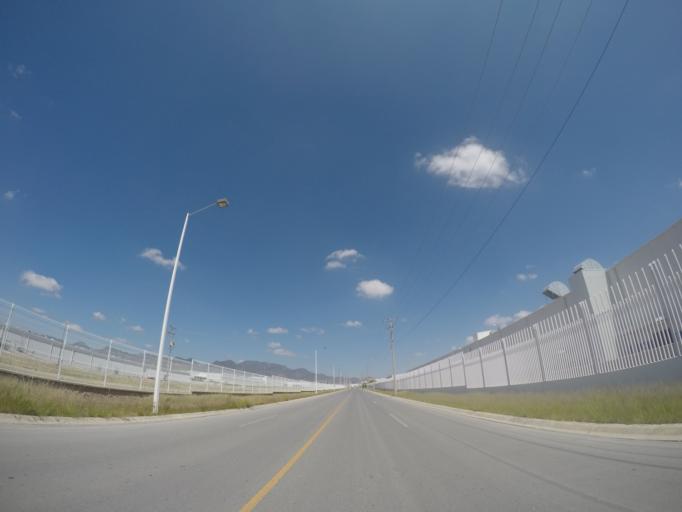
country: MX
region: San Luis Potosi
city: La Pila
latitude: 21.9703
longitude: -100.8743
